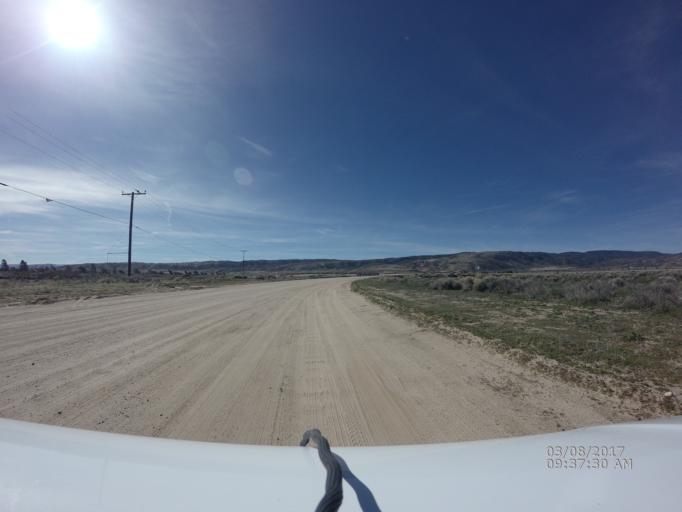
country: US
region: California
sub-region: Los Angeles County
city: Green Valley
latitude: 34.7466
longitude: -118.4664
